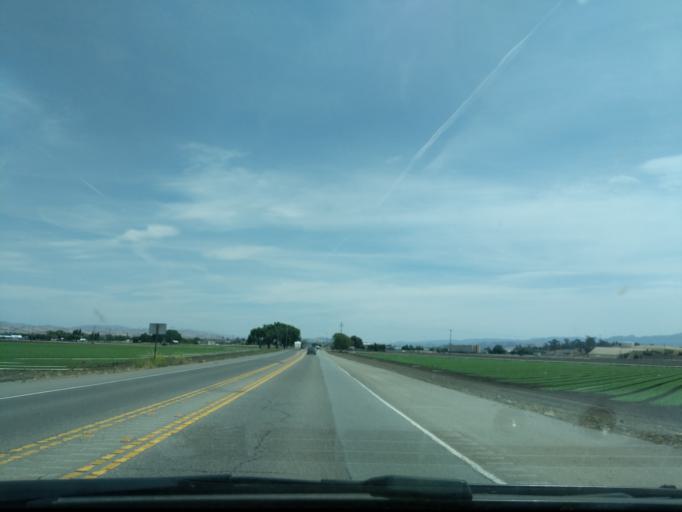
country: US
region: California
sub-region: San Benito County
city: Hollister
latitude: 36.8719
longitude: -121.4085
